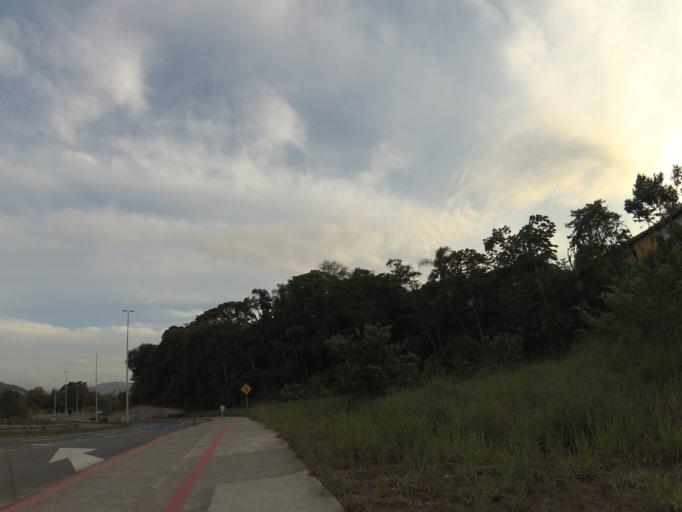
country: BR
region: Santa Catarina
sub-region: Blumenau
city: Blumenau
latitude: -26.8872
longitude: -49.1412
